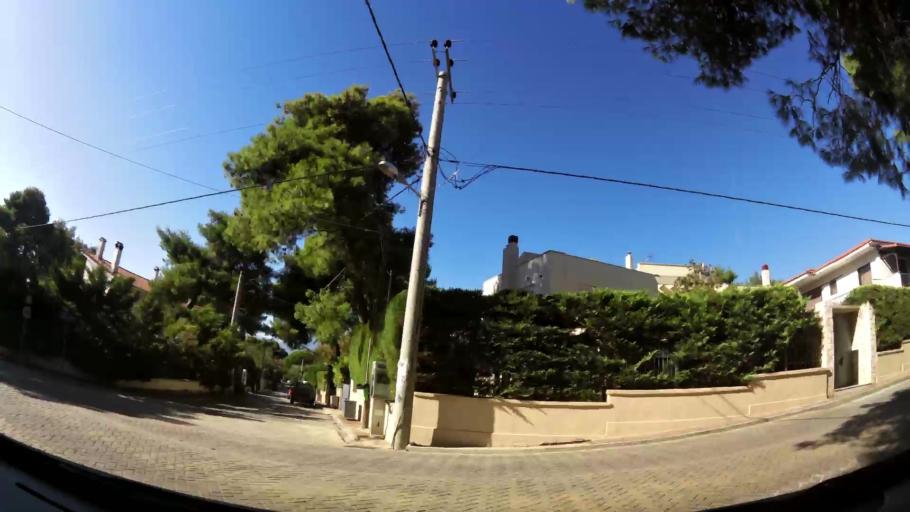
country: GR
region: Attica
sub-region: Nomarchia Athinas
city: Ekali
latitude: 38.1171
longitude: 23.8385
